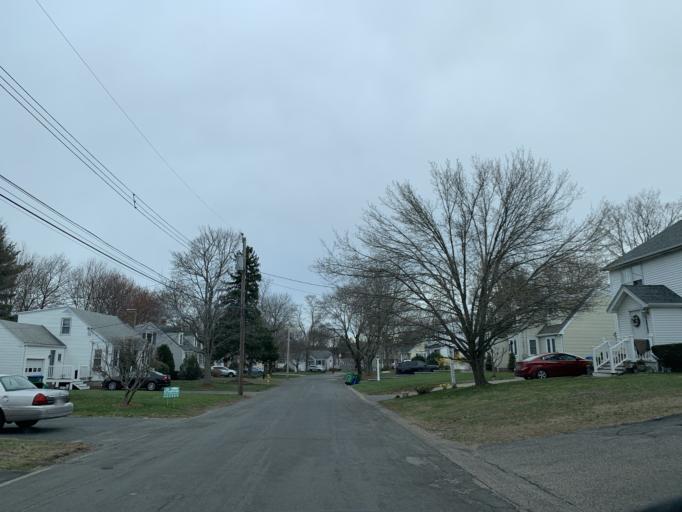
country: US
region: Massachusetts
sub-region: Norfolk County
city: Dedham
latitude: 42.2187
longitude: -71.1824
